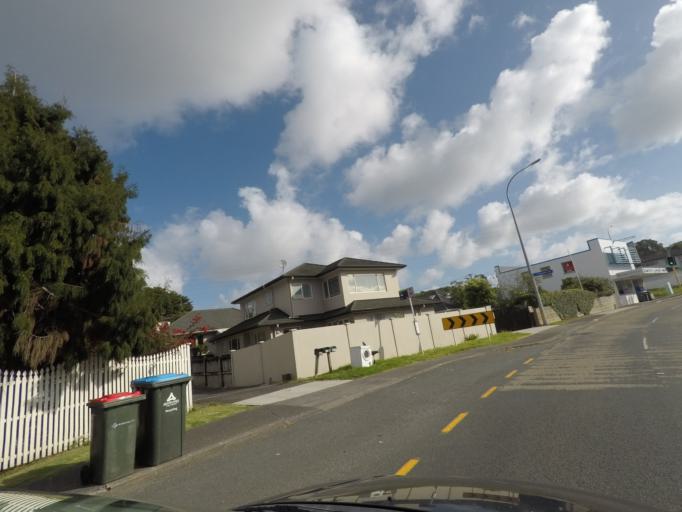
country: NZ
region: Auckland
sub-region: Auckland
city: Auckland
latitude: -36.9196
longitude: 174.7580
